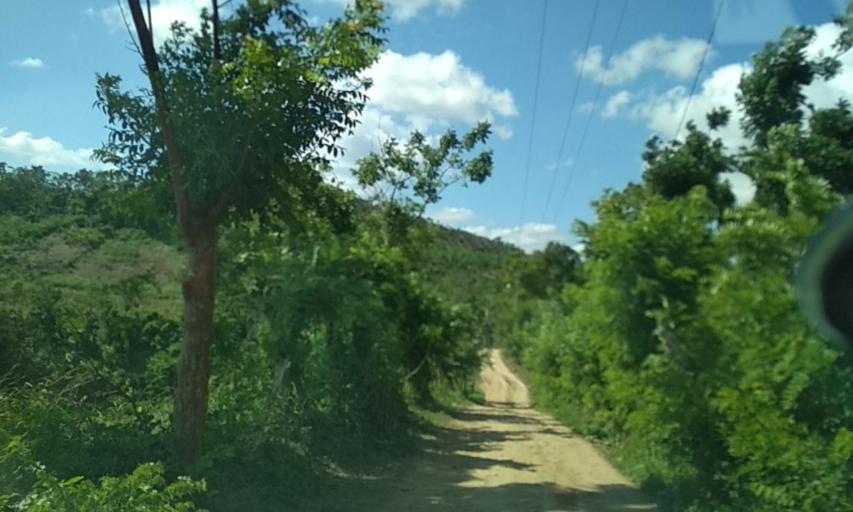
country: MX
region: Veracruz
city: Cazones de Herrera
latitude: 20.6227
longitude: -97.3309
